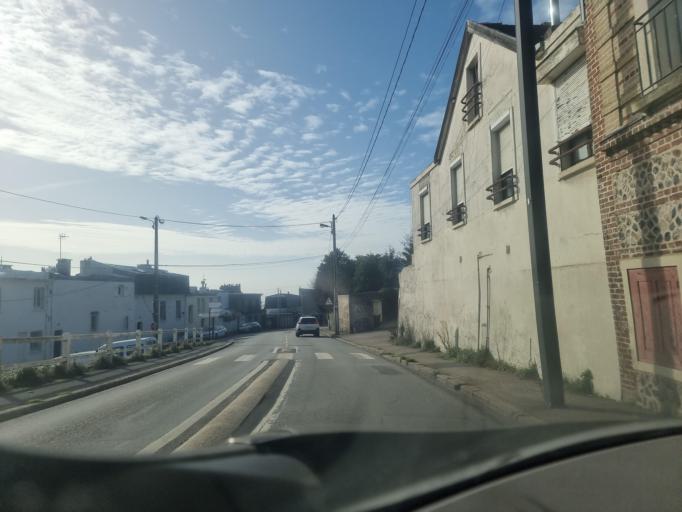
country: FR
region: Haute-Normandie
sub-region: Departement de la Seine-Maritime
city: Sainte-Adresse
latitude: 49.5016
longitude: 0.0956
